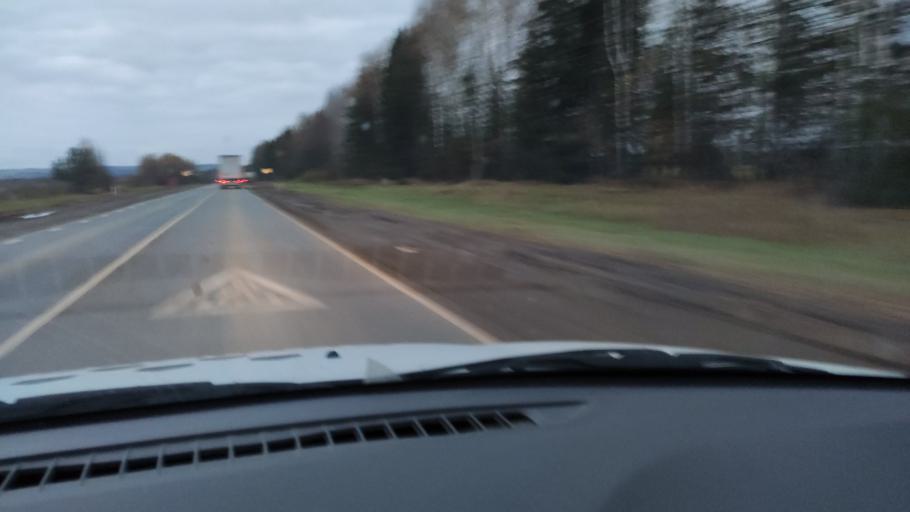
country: RU
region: Kirov
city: Kostino
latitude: 58.8580
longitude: 53.1832
